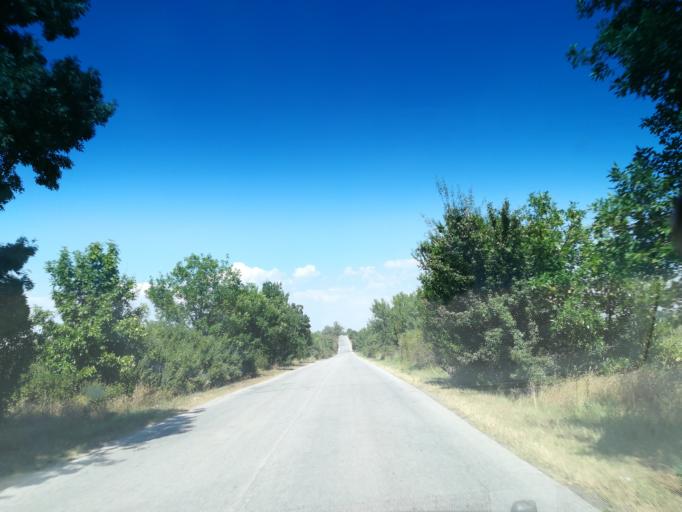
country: BG
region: Plovdiv
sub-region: Obshtina Sadovo
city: Sadovo
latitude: 42.0532
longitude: 25.1499
